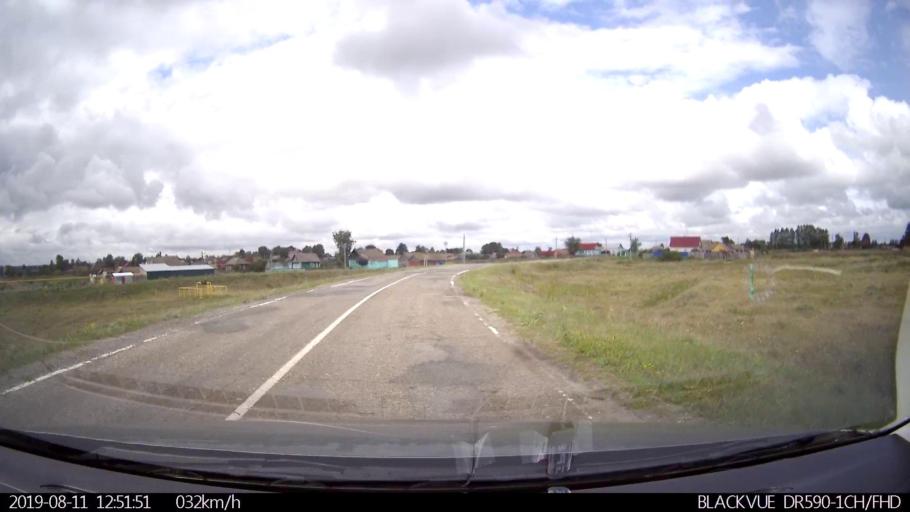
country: RU
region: Ulyanovsk
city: Ignatovka
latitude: 53.8767
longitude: 47.6625
